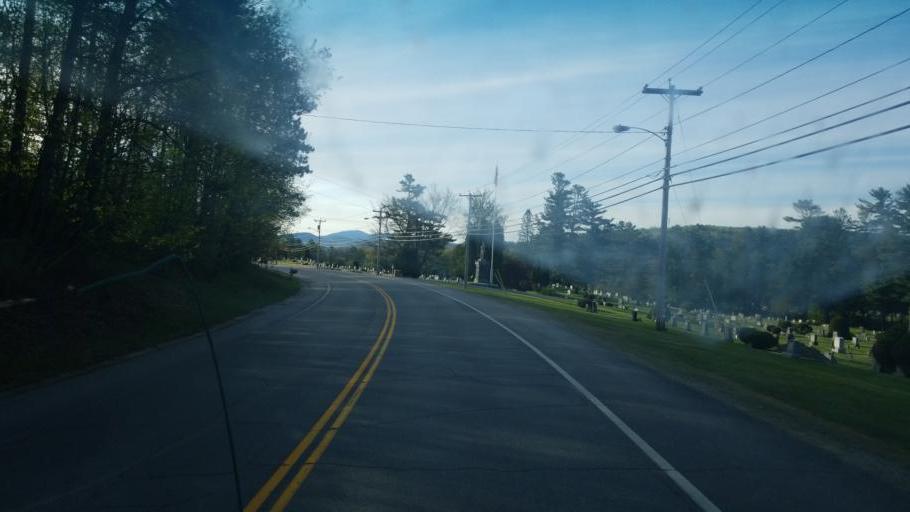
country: US
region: New Hampshire
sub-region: Grafton County
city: Littleton
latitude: 44.3126
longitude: -71.7931
